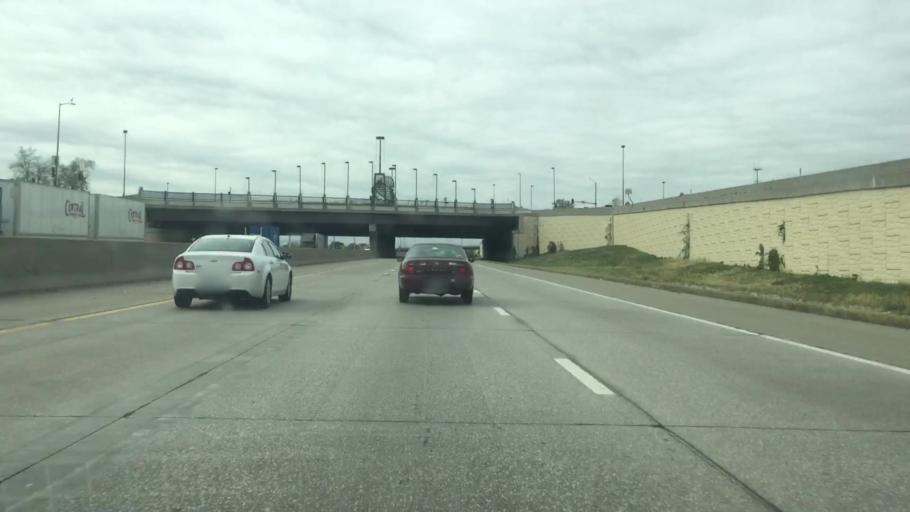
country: US
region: Kansas
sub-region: Johnson County
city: Lenexa
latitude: 38.9726
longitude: -94.7176
